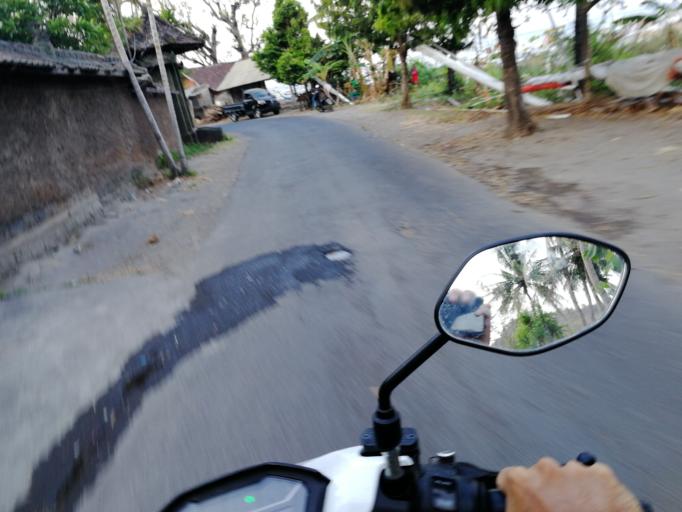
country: ID
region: Bali
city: Biaslantang Kaler
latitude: -8.3545
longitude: 115.6881
